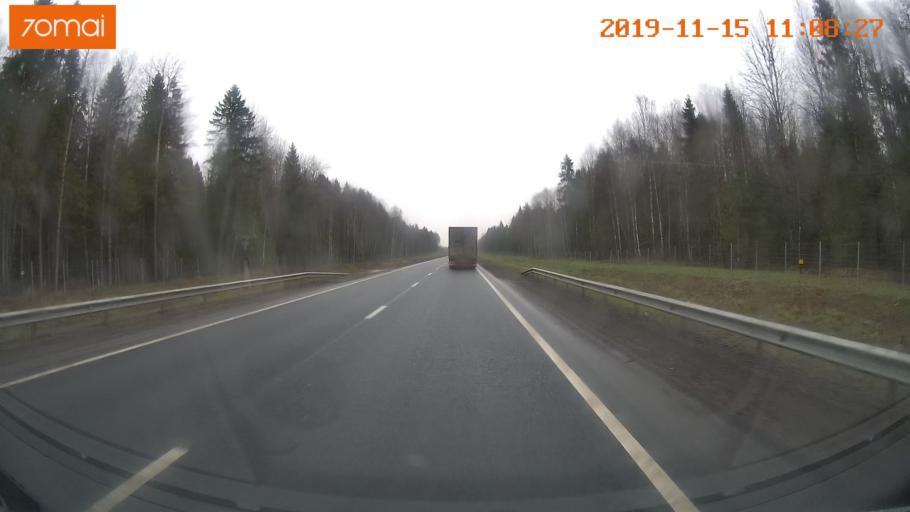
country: RU
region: Vologda
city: Chebsara
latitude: 59.1200
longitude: 39.0747
